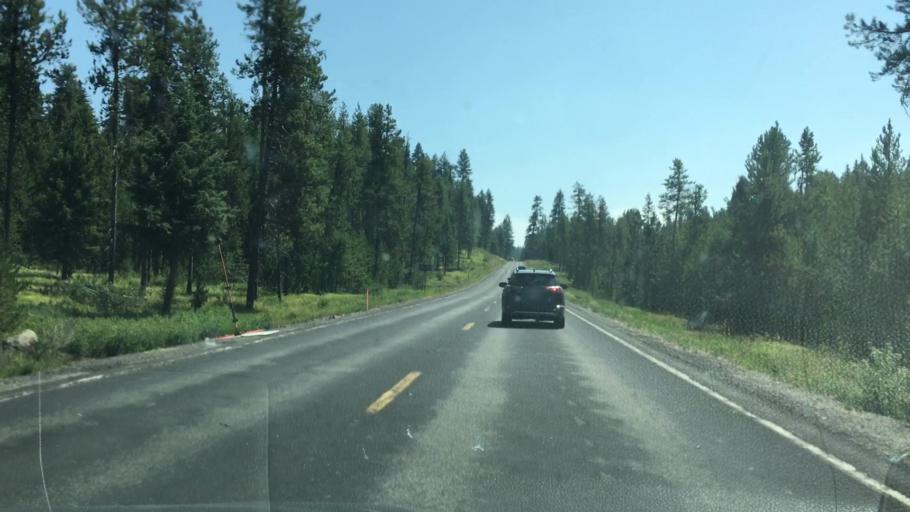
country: US
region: Idaho
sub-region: Valley County
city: McCall
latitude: 44.9467
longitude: -116.1680
